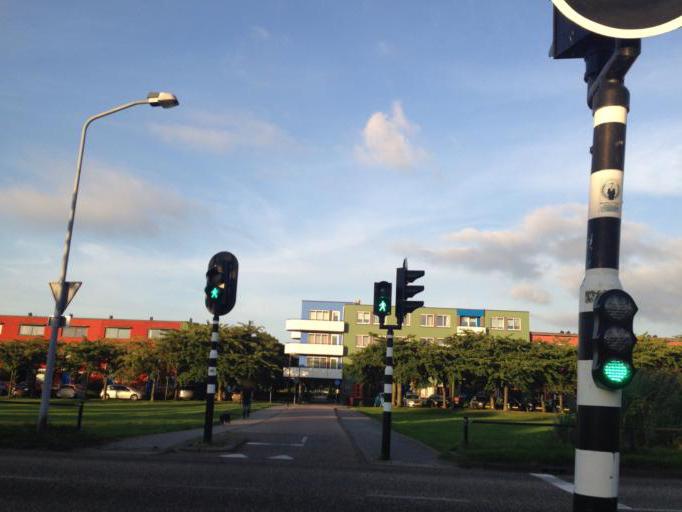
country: NL
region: Flevoland
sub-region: Gemeente Almere
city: Almere Stad
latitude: 52.3940
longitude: 5.2957
